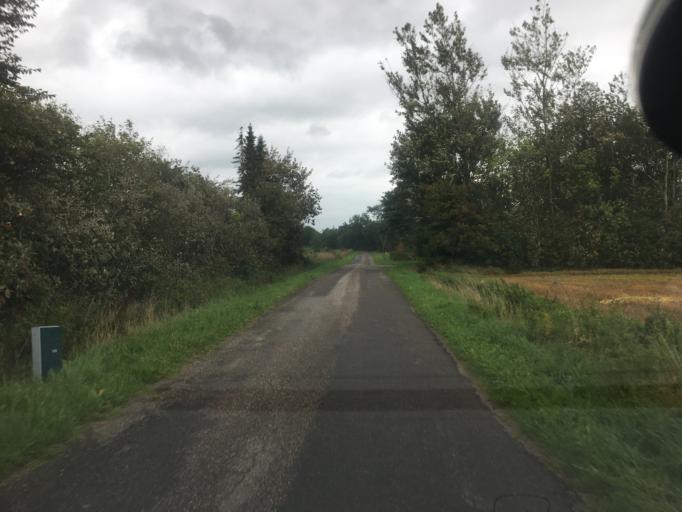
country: DK
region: South Denmark
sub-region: Tonder Kommune
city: Tonder
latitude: 54.9800
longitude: 8.9306
